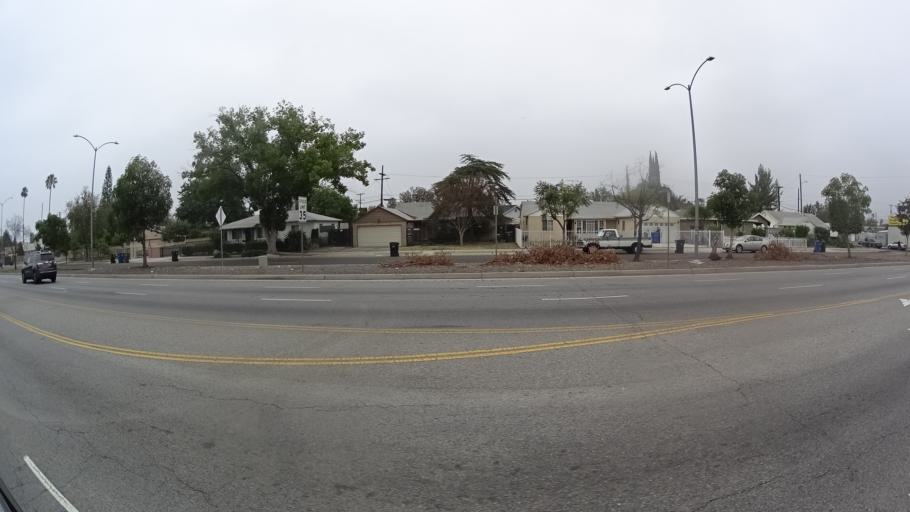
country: US
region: California
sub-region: Los Angeles County
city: North Hollywood
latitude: 34.1867
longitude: -118.4111
